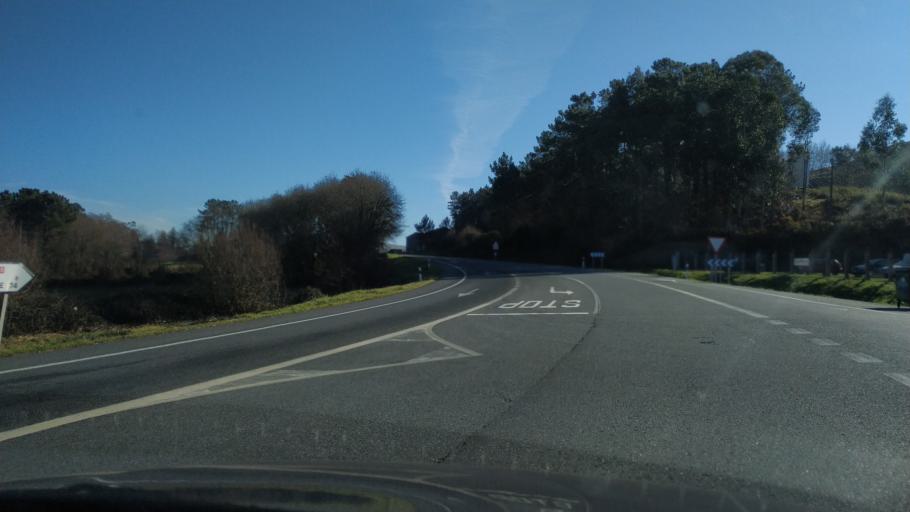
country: ES
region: Galicia
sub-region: Provincia da Coruna
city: Ribeira
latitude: 42.7483
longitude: -8.3459
